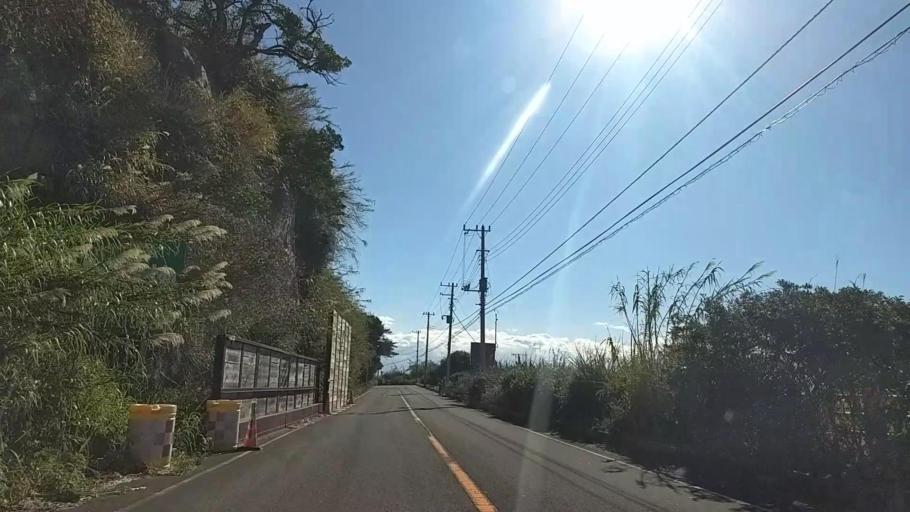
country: JP
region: Chiba
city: Tateyama
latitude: 34.9102
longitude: 139.8299
